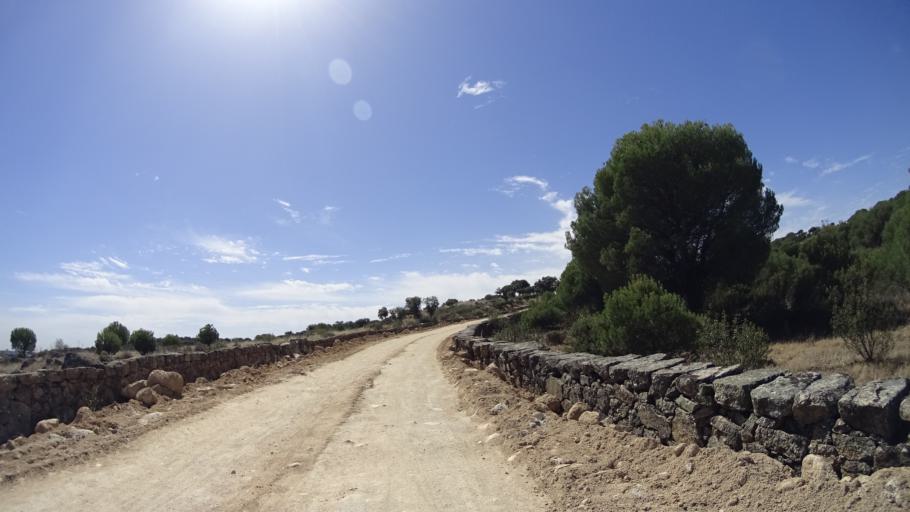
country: ES
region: Madrid
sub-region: Provincia de Madrid
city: Torrelodones
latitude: 40.5672
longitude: -3.9388
